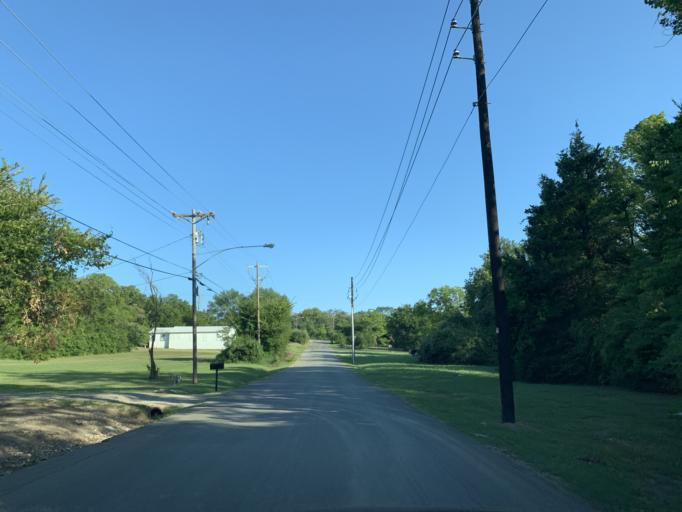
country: US
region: Texas
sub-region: Dallas County
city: Hutchins
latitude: 32.6699
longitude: -96.7736
